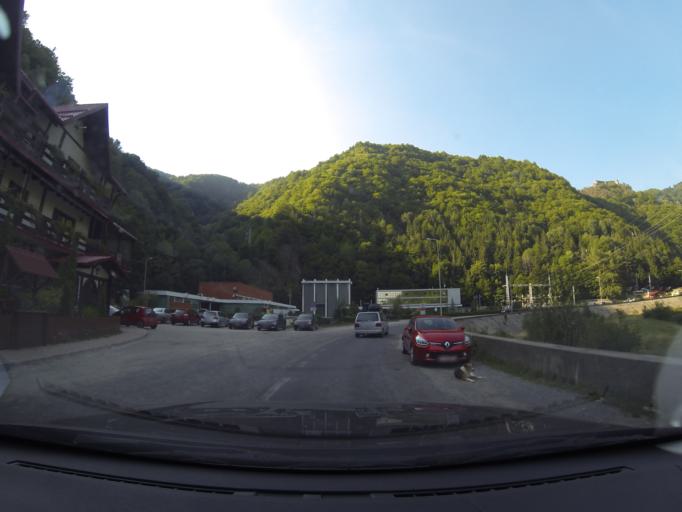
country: RO
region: Arges
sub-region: Comuna Arefu
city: Arefu
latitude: 45.3484
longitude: 24.6319
